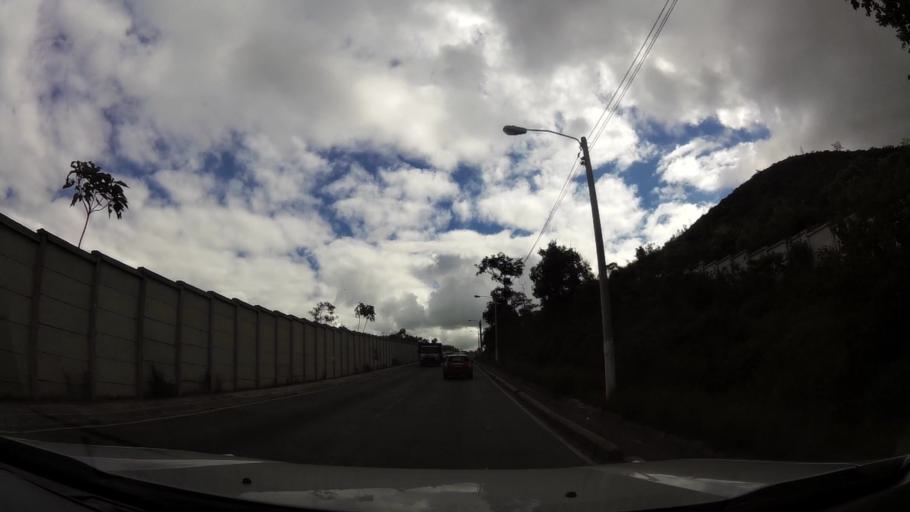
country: GT
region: Guatemala
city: Guatemala City
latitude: 14.6660
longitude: -90.5522
